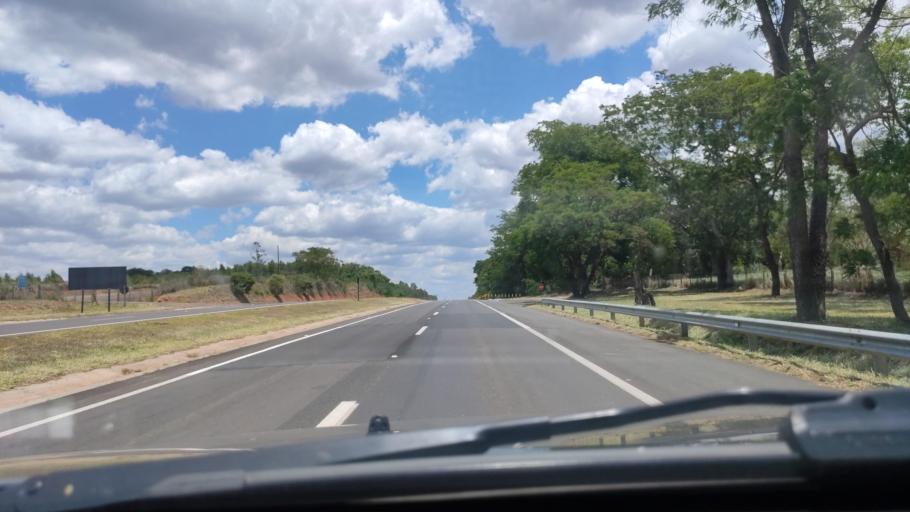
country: BR
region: Sao Paulo
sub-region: Duartina
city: Duartina
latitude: -22.5074
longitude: -49.2925
